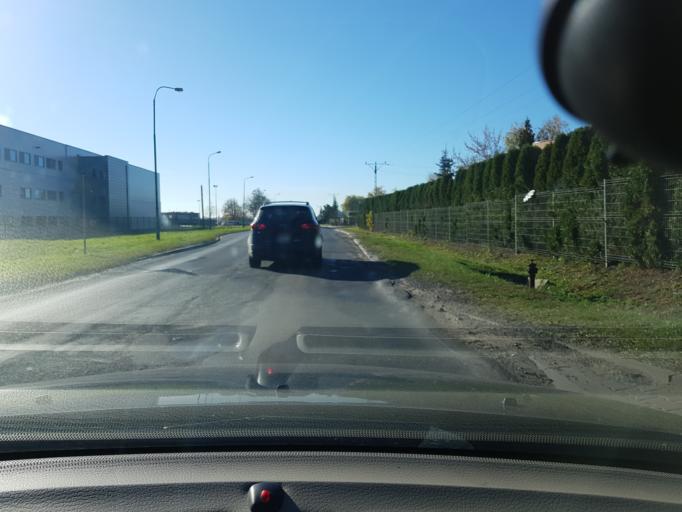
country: PL
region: Lodz Voivodeship
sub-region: Powiat tomaszowski
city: Tomaszow Mazowiecki
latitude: 51.5602
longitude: 20.0206
